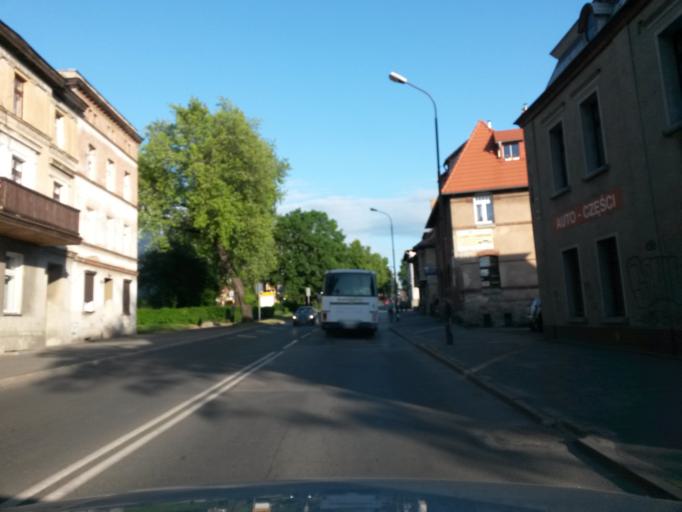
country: PL
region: Lower Silesian Voivodeship
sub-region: Jelenia Gora
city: Jelenia Gora
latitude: 50.8984
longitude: 15.7413
